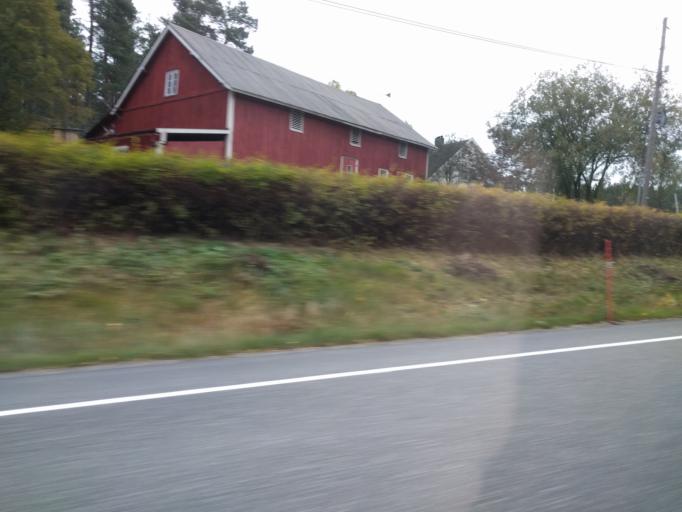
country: NO
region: Aust-Agder
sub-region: Evje og Hornnes
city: Evje
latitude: 58.4896
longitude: 7.7766
